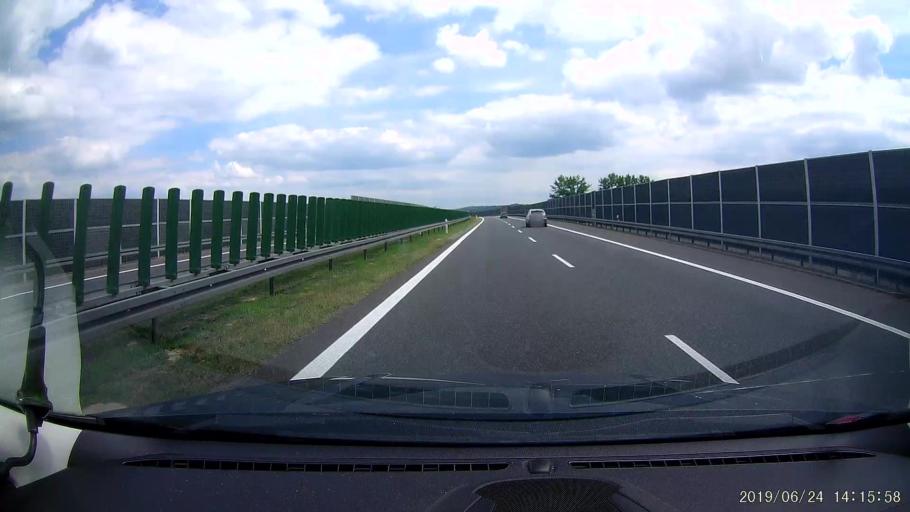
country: PL
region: Lesser Poland Voivodeship
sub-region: Powiat wielicki
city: Klaj
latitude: 49.9842
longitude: 20.3063
